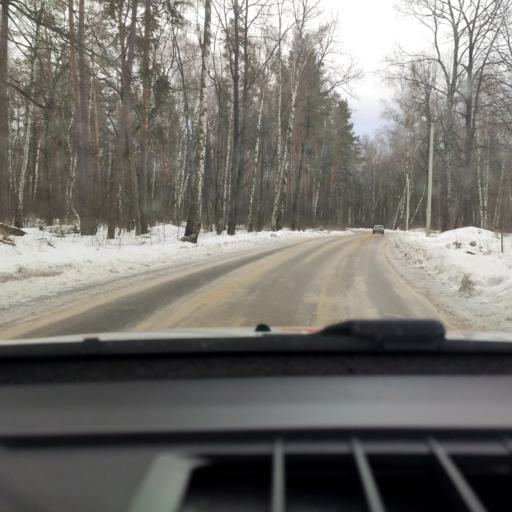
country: RU
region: Voronezj
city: Podgornoye
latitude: 51.7541
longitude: 39.1530
